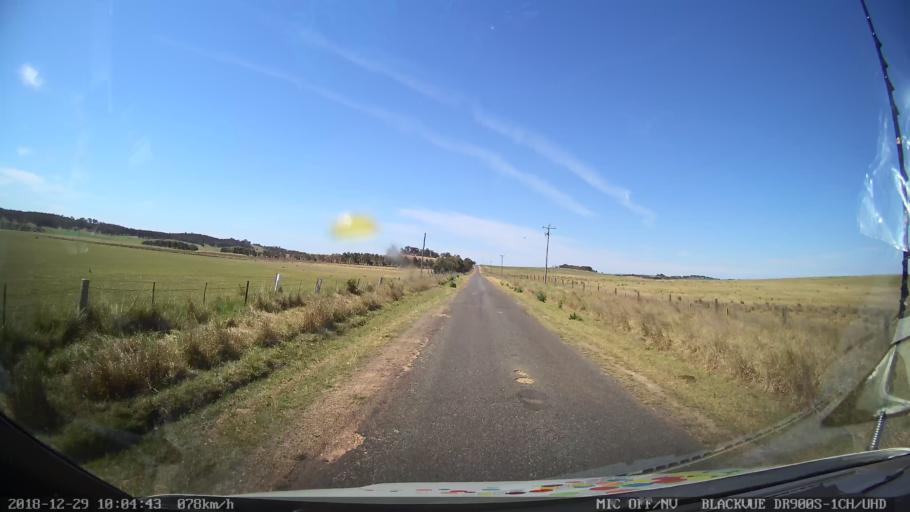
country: AU
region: New South Wales
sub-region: Goulburn Mulwaree
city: Goulburn
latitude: -34.8252
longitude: 149.4548
